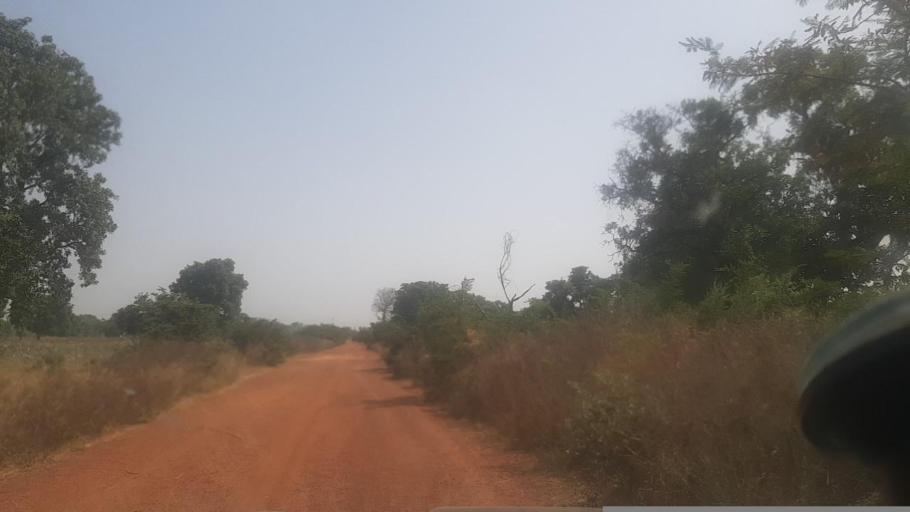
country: ML
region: Segou
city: Bla
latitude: 12.9161
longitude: -6.2520
